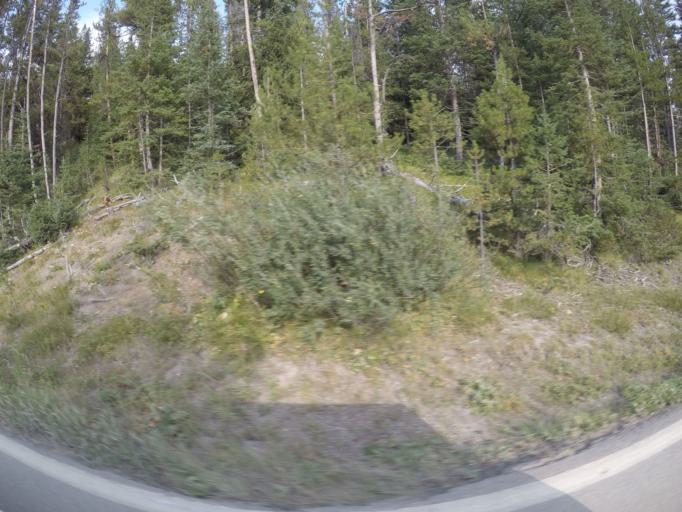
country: US
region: Montana
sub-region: Gallatin County
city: West Yellowstone
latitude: 44.8661
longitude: -110.7373
